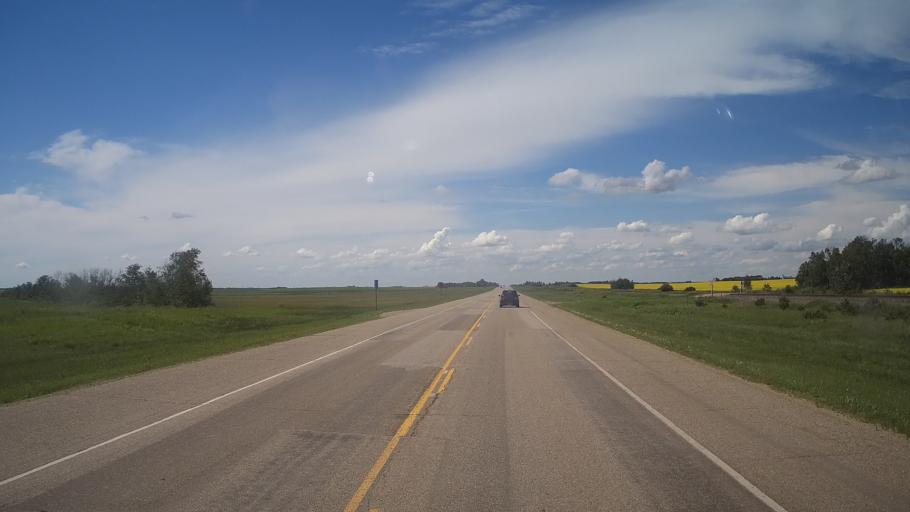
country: CA
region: Saskatchewan
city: Yorkton
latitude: 51.0772
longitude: -102.2394
